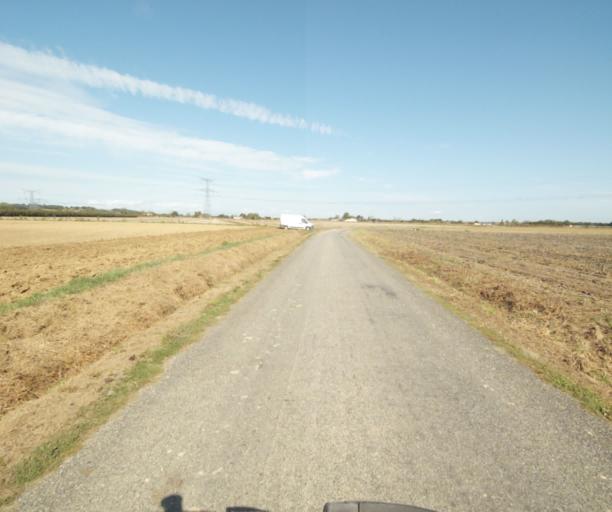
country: FR
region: Midi-Pyrenees
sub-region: Departement du Tarn-et-Garonne
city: Verdun-sur-Garonne
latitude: 43.8475
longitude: 1.2036
